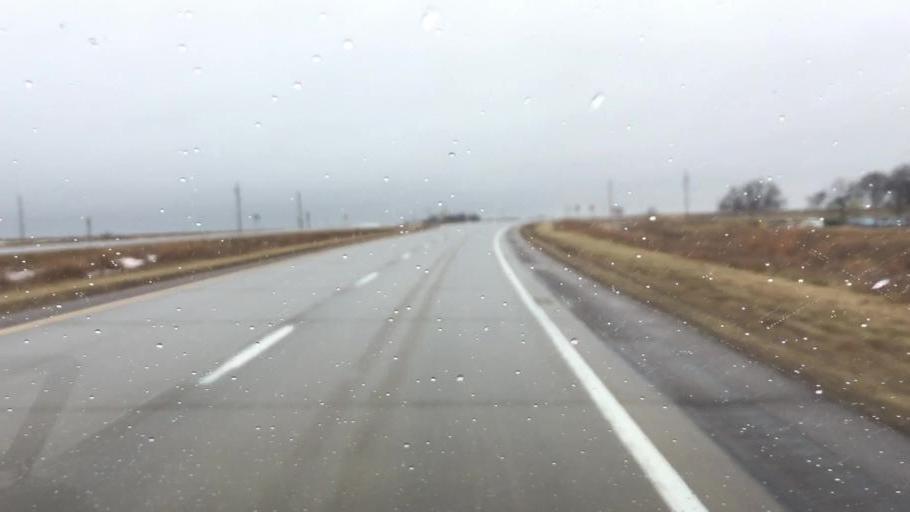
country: US
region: Iowa
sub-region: O'Brien County
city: Sheldon
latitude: 43.0710
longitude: -95.8969
